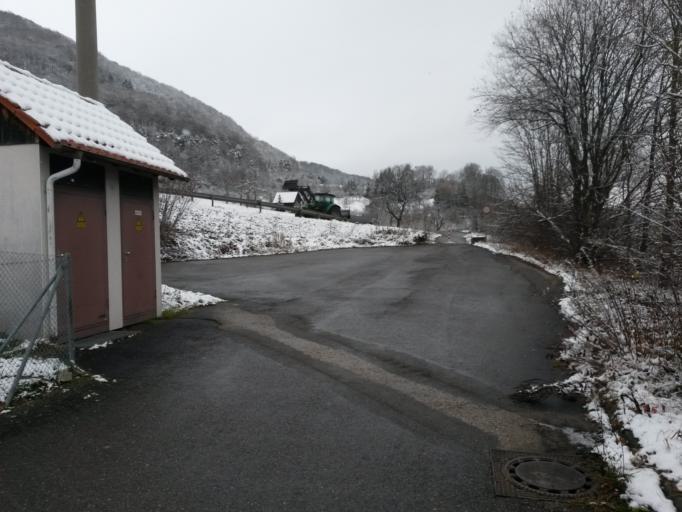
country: DE
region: Baden-Wuerttemberg
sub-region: Regierungsbezirk Stuttgart
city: Bad Uberkingen
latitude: 48.6046
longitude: 9.7969
